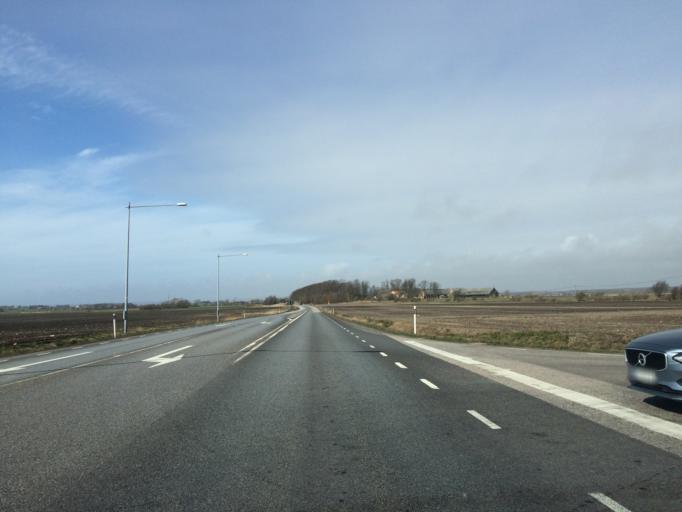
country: SE
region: Halland
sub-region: Halmstads Kommun
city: Paarp
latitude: 56.5972
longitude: 12.9734
